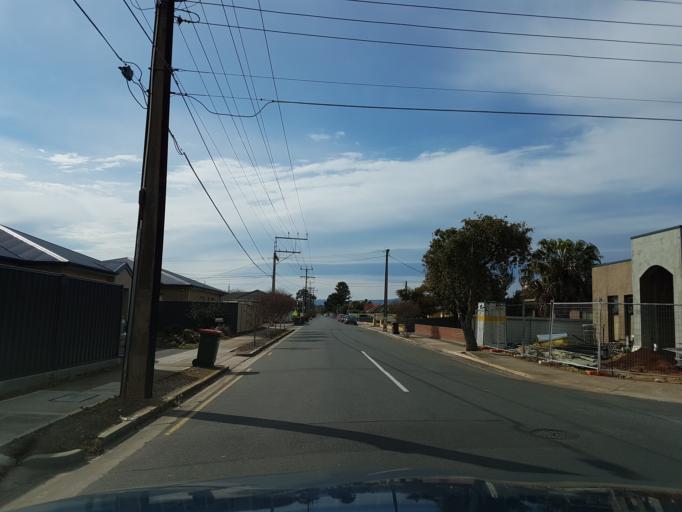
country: AU
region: South Australia
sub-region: City of West Torrens
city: Plympton
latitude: -34.9309
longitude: 138.5375
